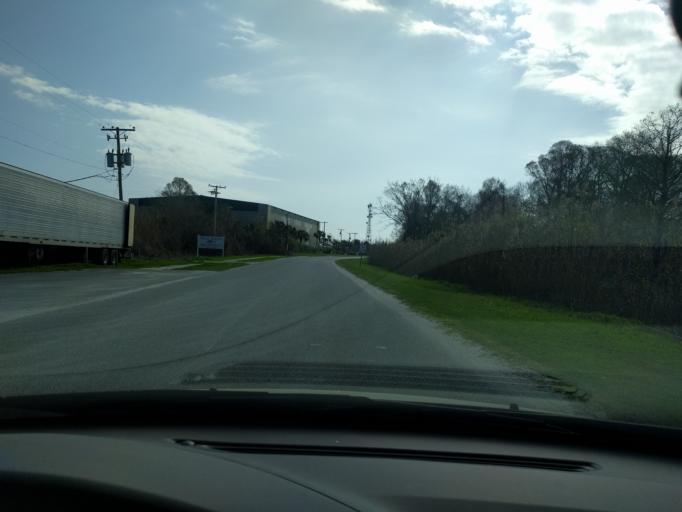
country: US
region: Florida
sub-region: Franklin County
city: Apalachicola
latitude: 29.7326
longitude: -84.9926
